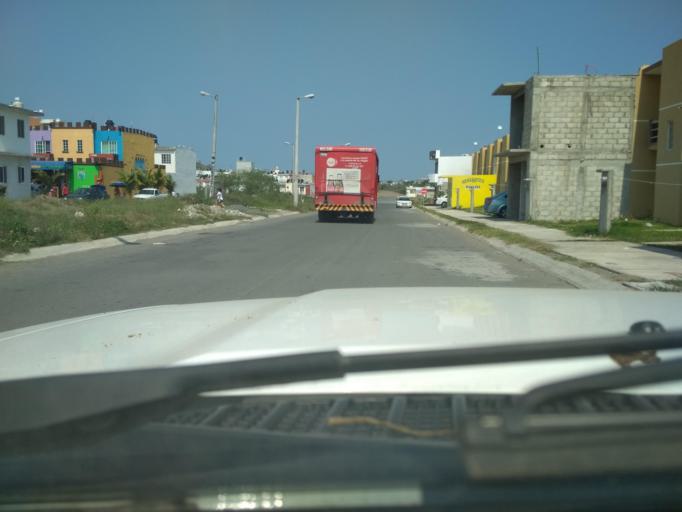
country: MX
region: Veracruz
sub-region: Veracruz
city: Lomas de Rio Medio Cuatro
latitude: 19.1909
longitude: -96.2094
